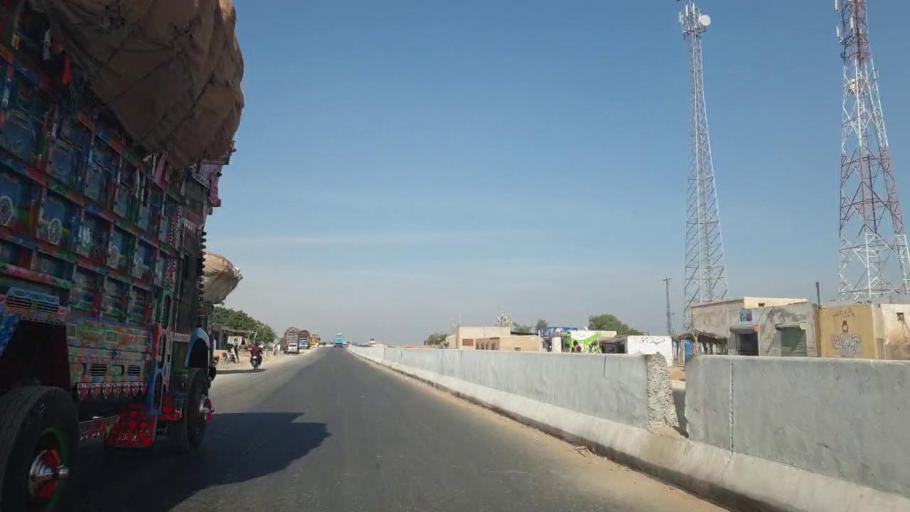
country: PK
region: Sindh
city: Matiari
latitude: 25.6492
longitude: 68.3010
